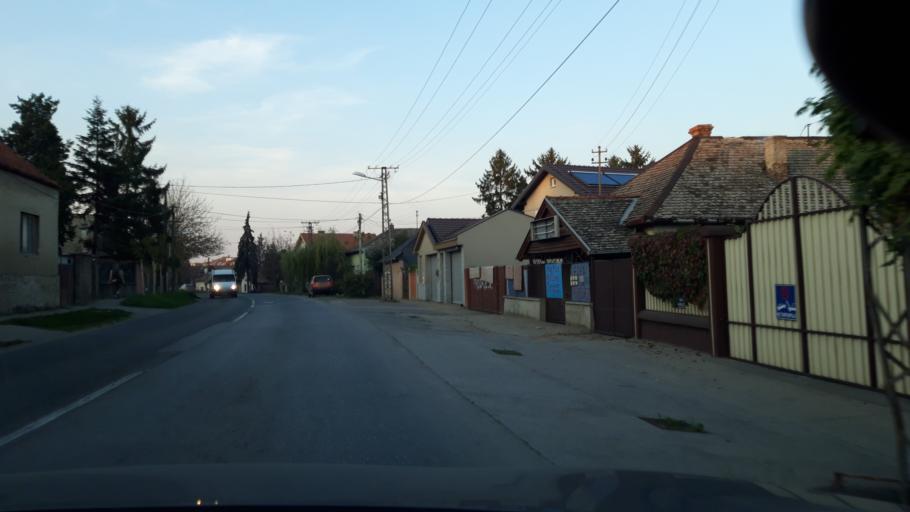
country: RS
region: Autonomna Pokrajina Vojvodina
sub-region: Juznobacki Okrug
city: Petrovaradin
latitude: 45.2352
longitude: 19.8849
